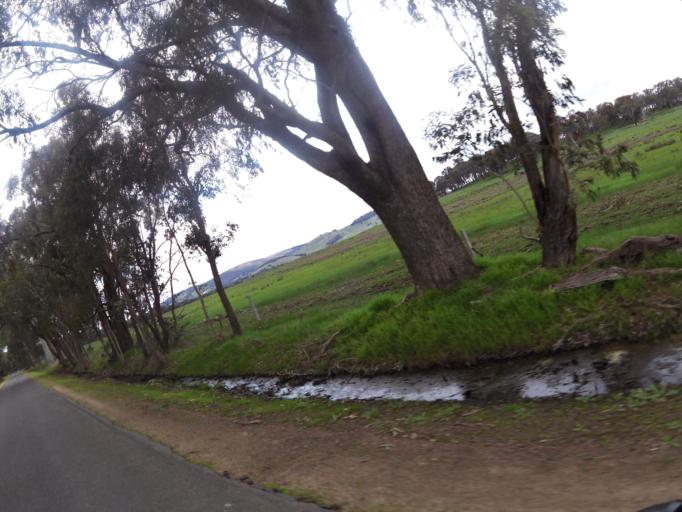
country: AU
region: Victoria
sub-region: Benalla
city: Benalla
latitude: -36.6559
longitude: 145.9045
